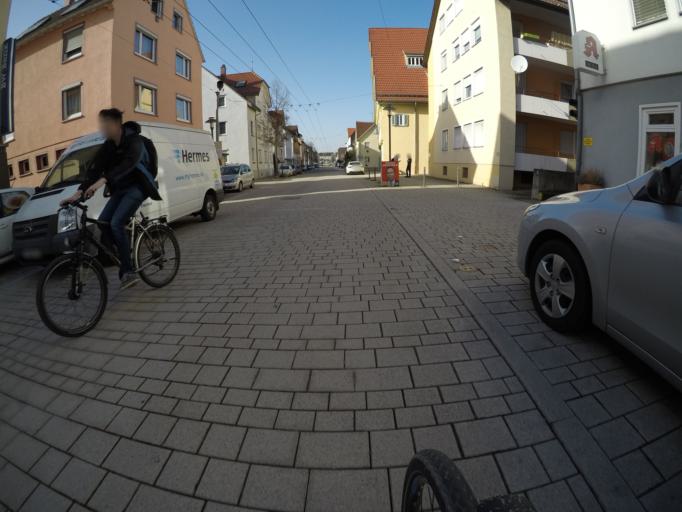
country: DE
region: Baden-Wuerttemberg
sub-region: Regierungsbezirk Stuttgart
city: Esslingen
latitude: 48.7468
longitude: 9.2782
